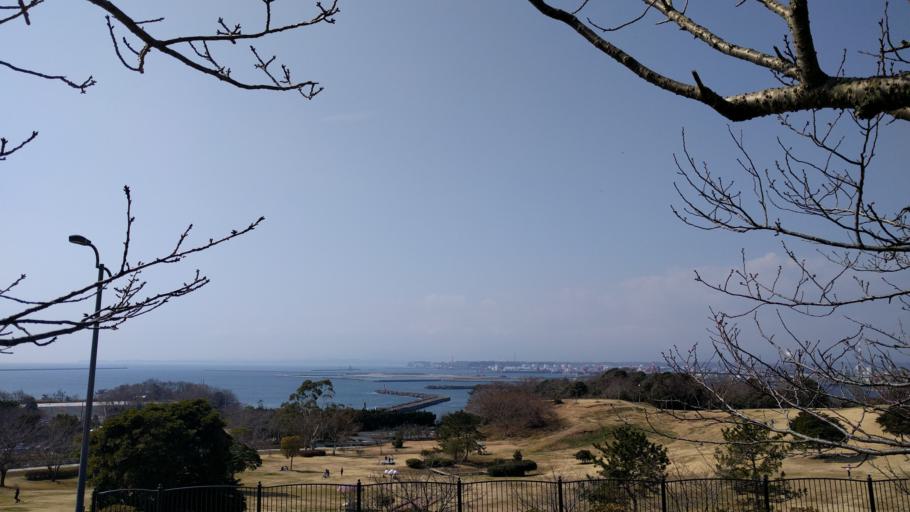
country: JP
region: Fukushima
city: Iwaki
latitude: 36.9388
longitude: 140.9196
